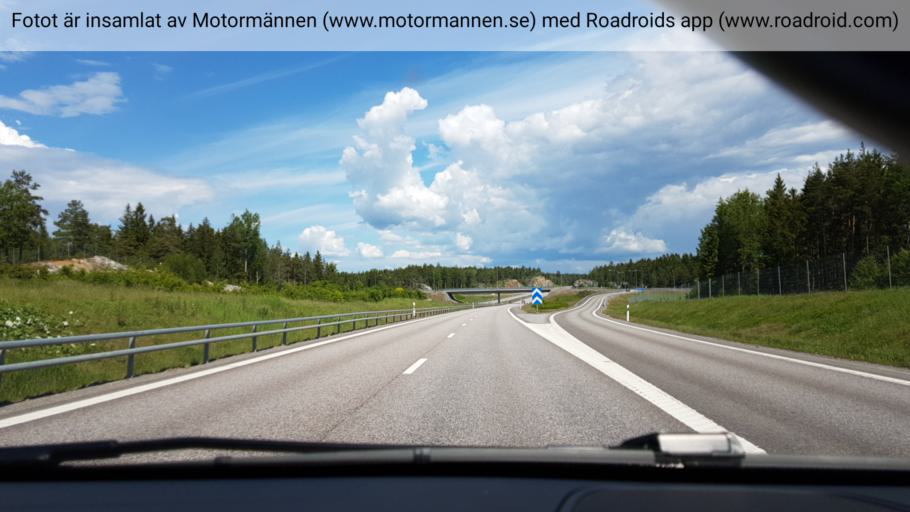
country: SE
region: Stockholm
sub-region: Nynashamns Kommun
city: Osmo
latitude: 59.0227
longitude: 17.9493
